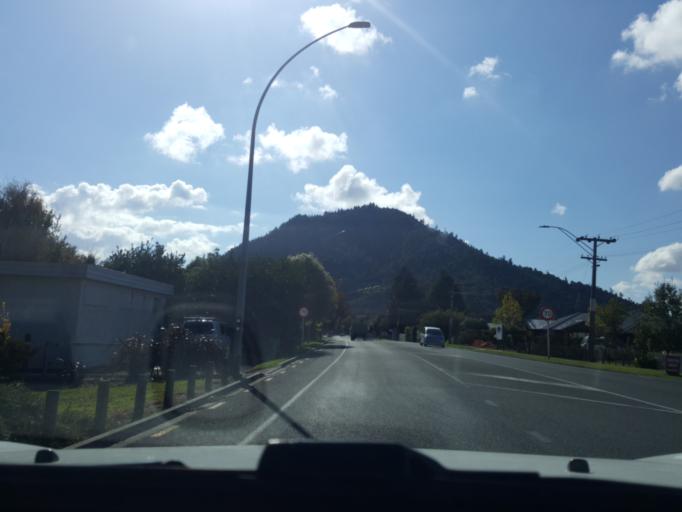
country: NZ
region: Waikato
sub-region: Waikato District
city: Ngaruawahia
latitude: -37.6161
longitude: 175.1867
